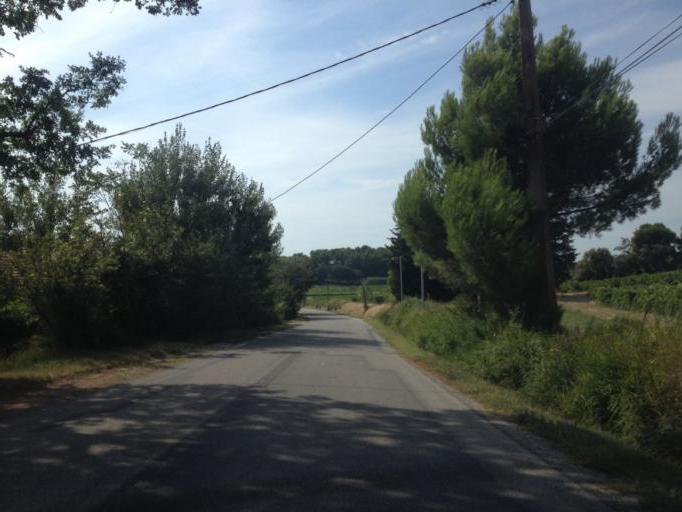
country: FR
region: Provence-Alpes-Cote d'Azur
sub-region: Departement du Vaucluse
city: Vacqueyras
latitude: 44.1378
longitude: 4.9993
